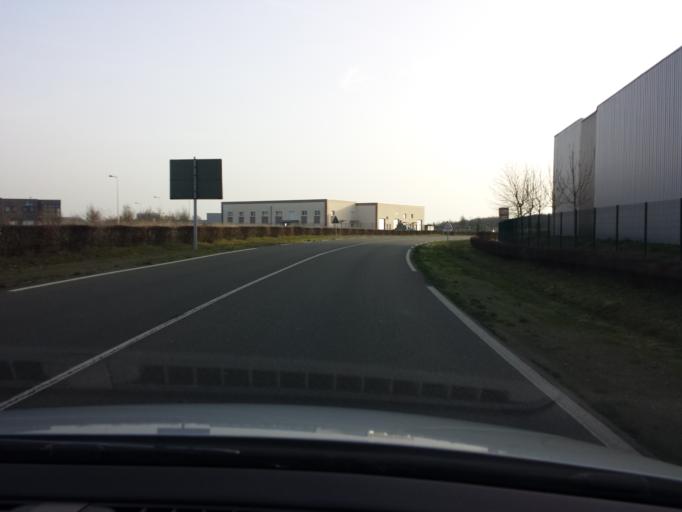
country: FR
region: Haute-Normandie
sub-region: Departement de l'Eure
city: Evreux
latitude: 49.0027
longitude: 1.1779
